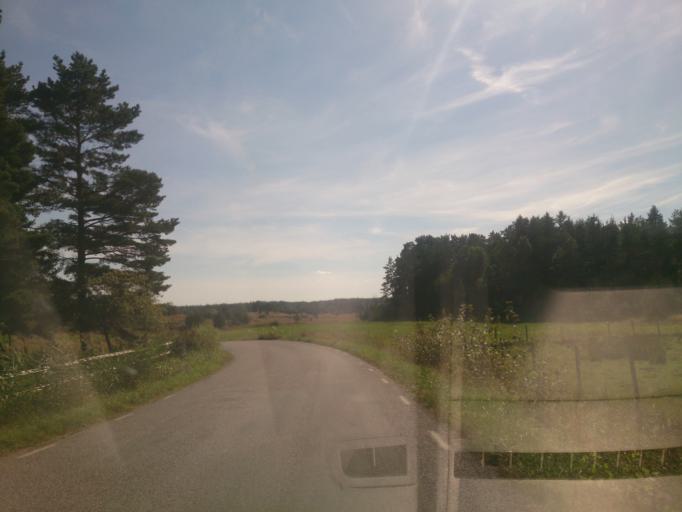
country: SE
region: OEstergoetland
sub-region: Norrkopings Kommun
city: Krokek
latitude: 58.5457
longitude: 16.5985
